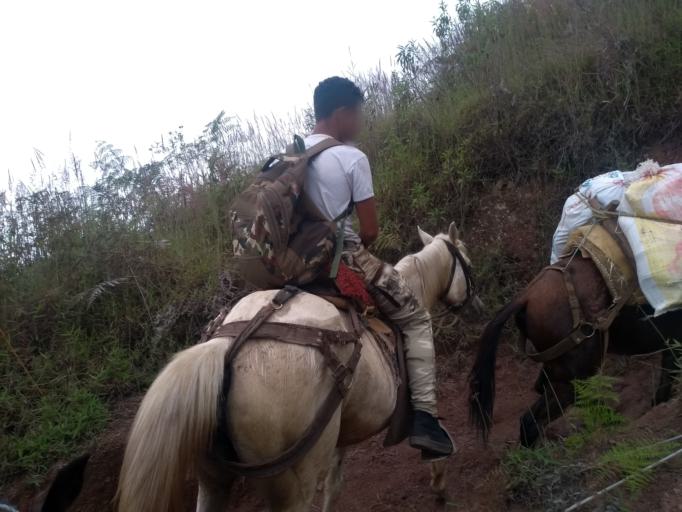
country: CO
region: Cesar
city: San Diego
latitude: 10.1789
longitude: -73.0384
